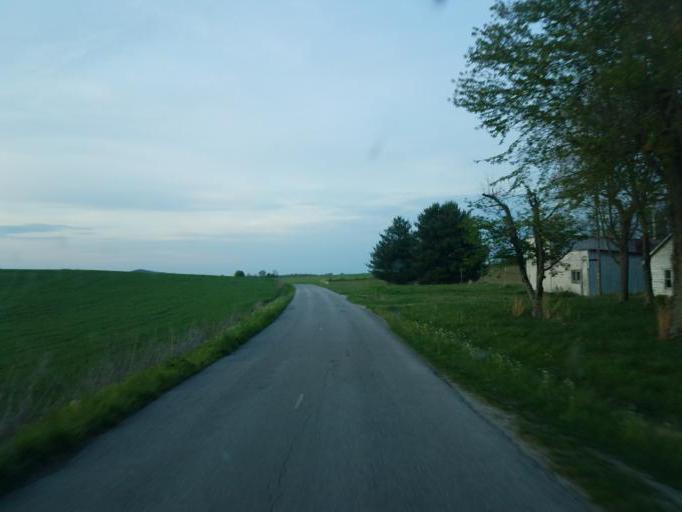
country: US
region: Kentucky
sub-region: Hart County
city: Munfordville
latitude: 37.2165
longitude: -85.6986
